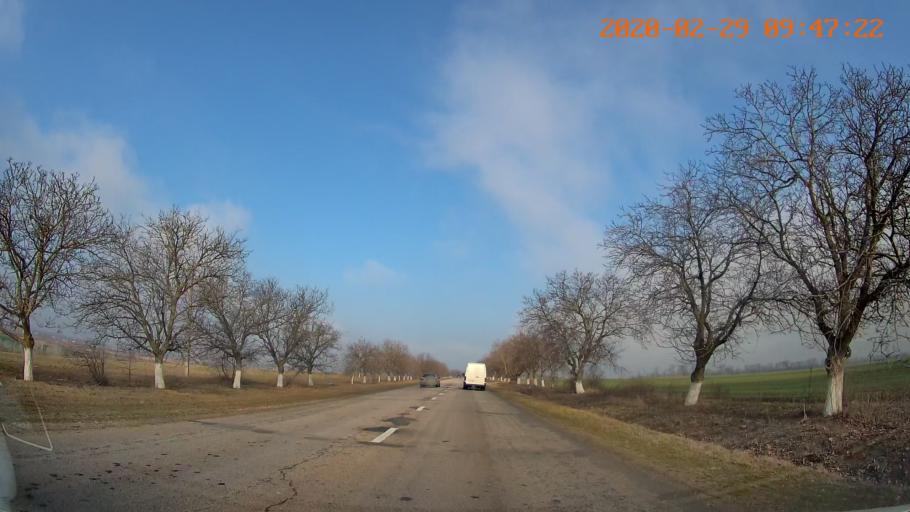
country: MD
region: Telenesti
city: Crasnoe
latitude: 46.6766
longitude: 29.7910
